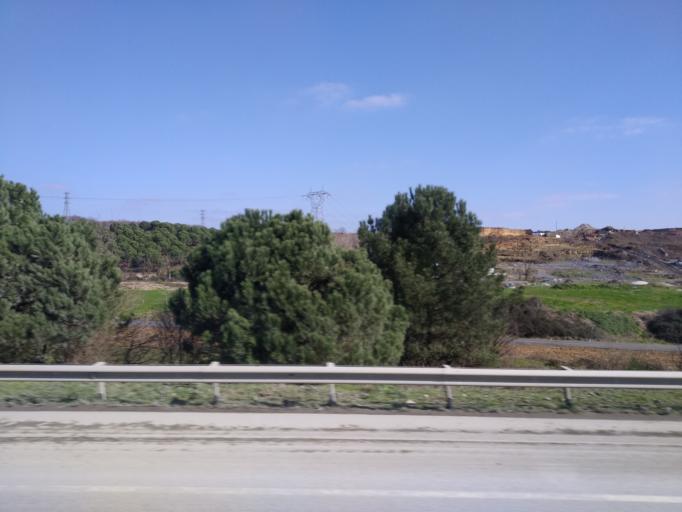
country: TR
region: Istanbul
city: Kemerburgaz
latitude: 41.1661
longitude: 28.8914
